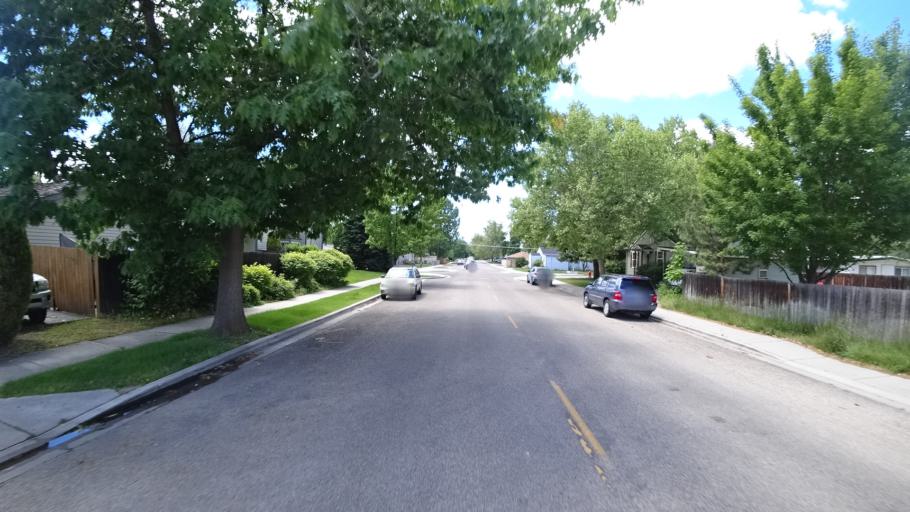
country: US
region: Idaho
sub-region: Ada County
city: Boise
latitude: 43.5946
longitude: -116.1905
